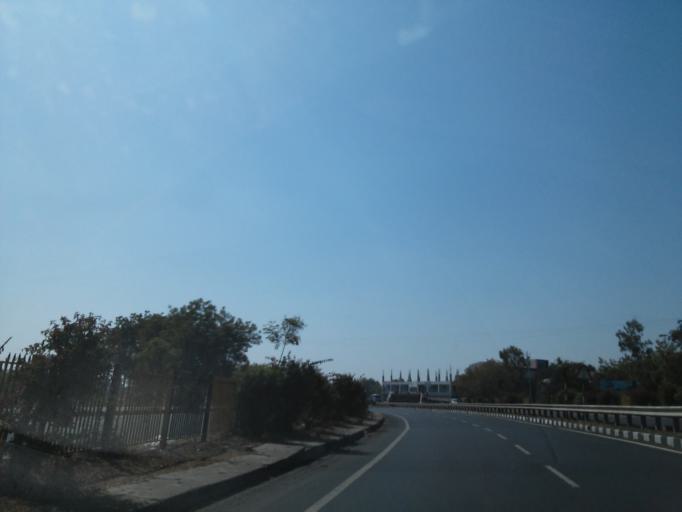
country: IN
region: Gujarat
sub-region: Gandhinagar
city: Chhala
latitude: 23.4428
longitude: 72.8459
